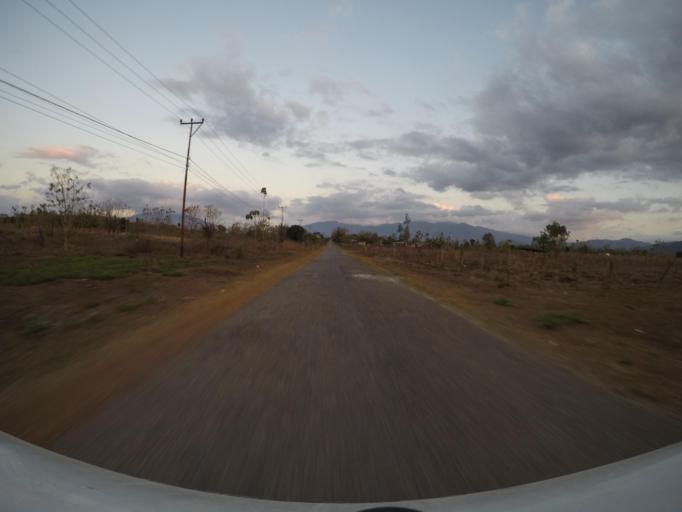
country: TL
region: Bobonaro
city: Maliana
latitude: -8.9714
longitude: 125.1330
